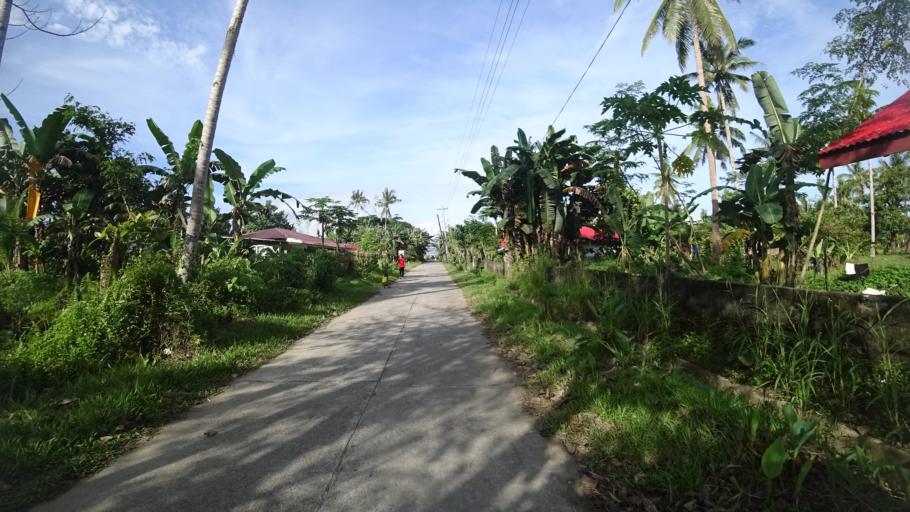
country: PH
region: Eastern Visayas
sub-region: Province of Leyte
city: Pastrana
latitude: 11.1556
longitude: 124.8606
